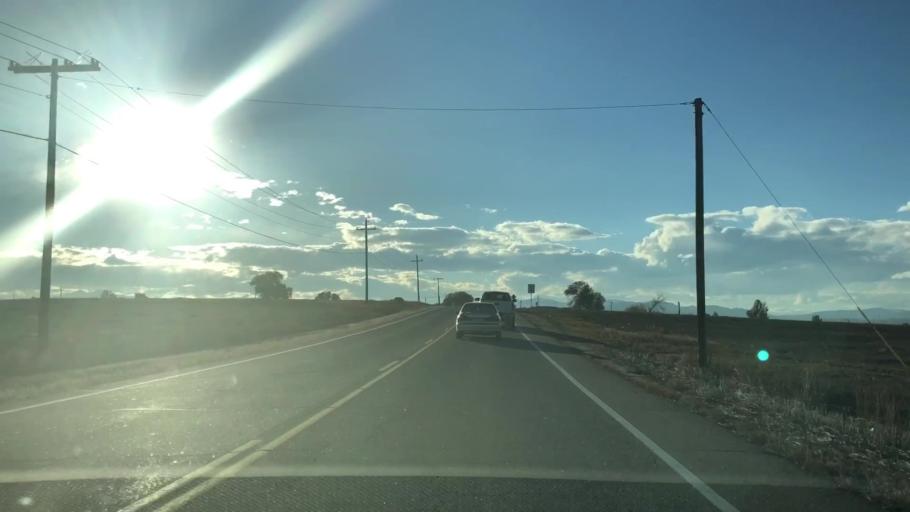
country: US
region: Colorado
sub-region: Larimer County
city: Loveland
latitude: 40.4803
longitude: -105.0356
